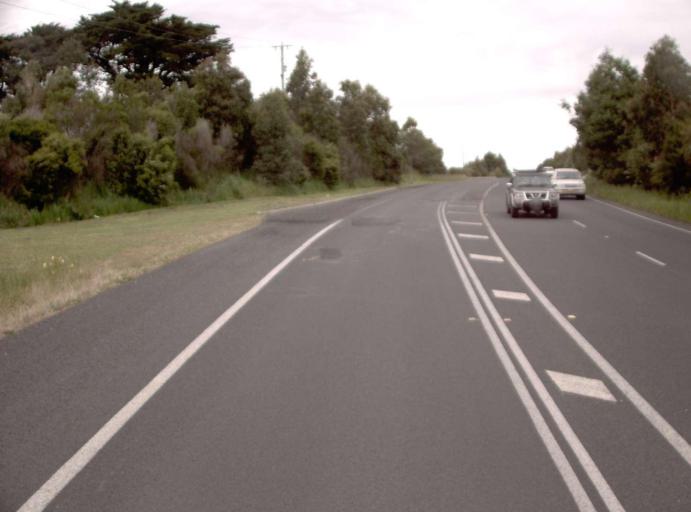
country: AU
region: Victoria
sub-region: Bass Coast
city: North Wonthaggi
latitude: -38.4005
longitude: 145.7575
